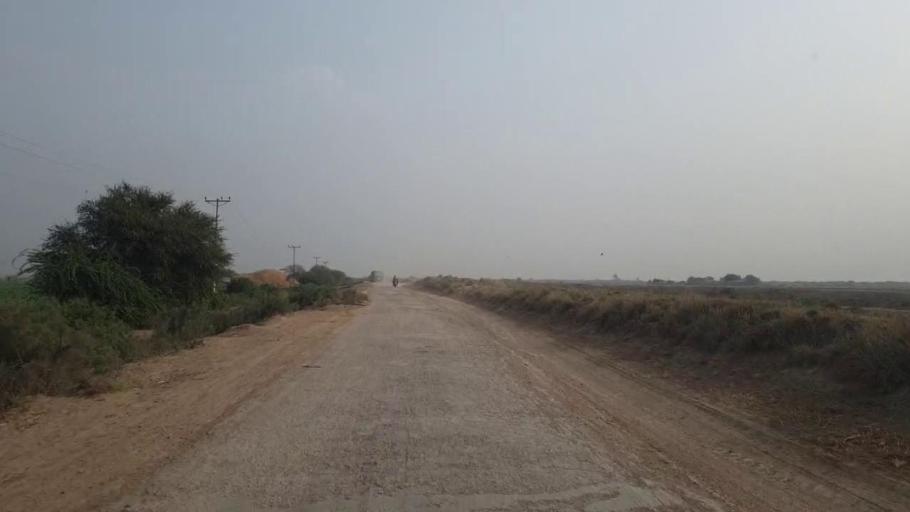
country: PK
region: Sindh
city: Mirpur Batoro
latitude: 24.5698
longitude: 68.3986
